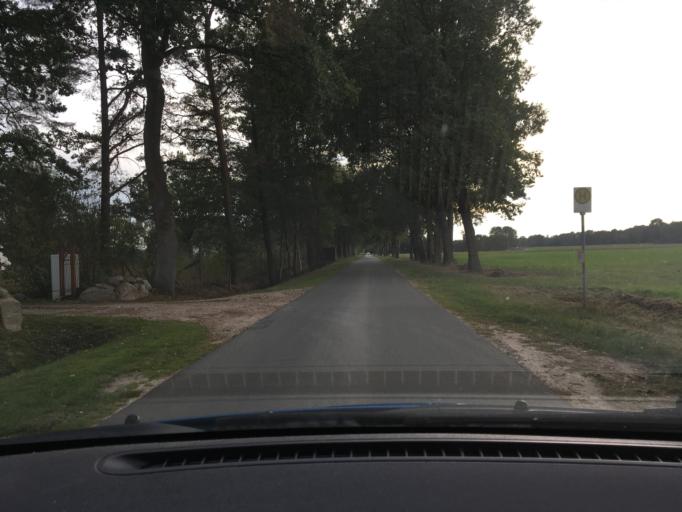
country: DE
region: Lower Saxony
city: Wietzendorf
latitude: 52.9002
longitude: 9.9589
